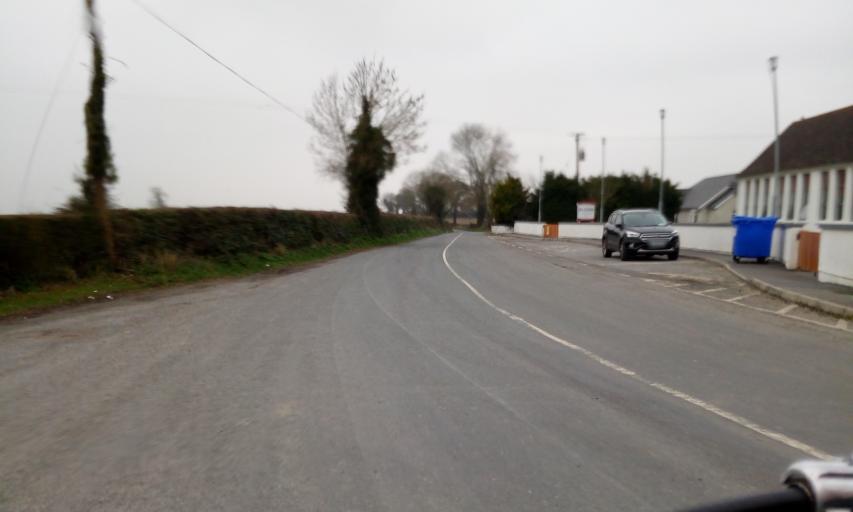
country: IE
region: Leinster
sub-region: Kilkenny
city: Kilkenny
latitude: 52.6576
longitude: -7.1535
